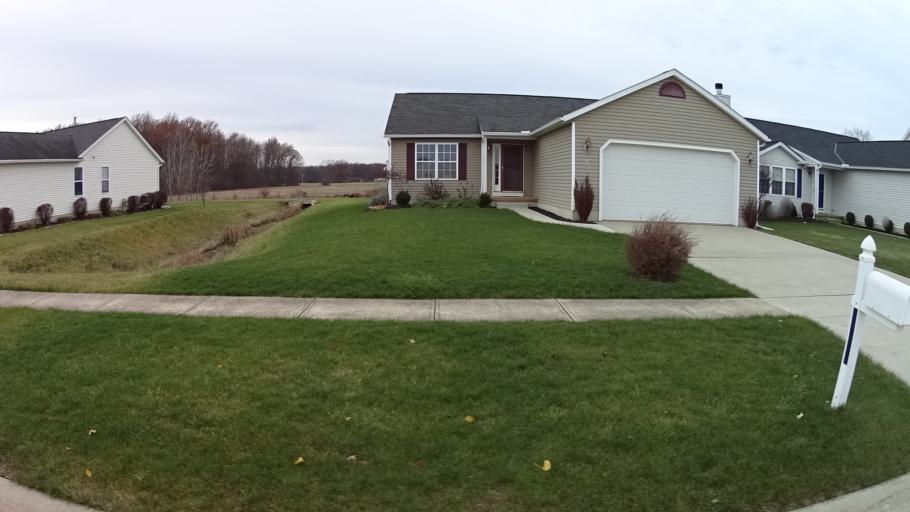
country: US
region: Ohio
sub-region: Lorain County
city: North Ridgeville
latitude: 41.4061
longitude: -82.0428
